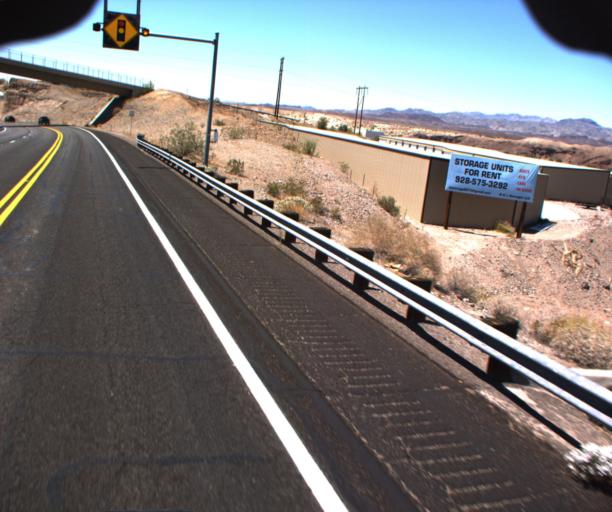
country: US
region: Arizona
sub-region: La Paz County
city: Cienega Springs
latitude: 34.1847
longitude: -114.2215
